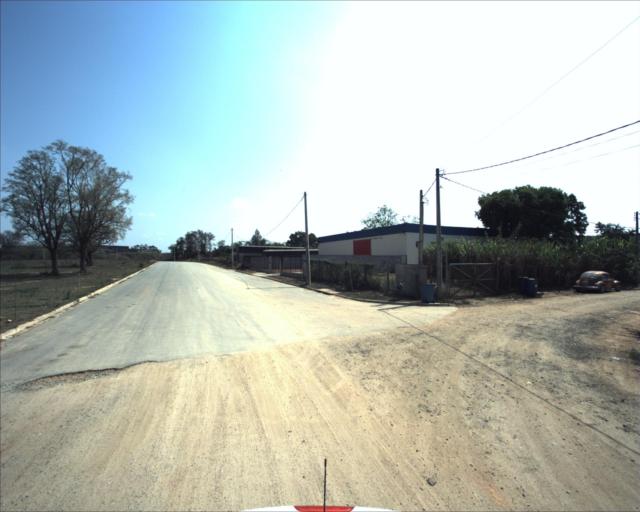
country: BR
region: Sao Paulo
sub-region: Sorocaba
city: Sorocaba
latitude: -23.4187
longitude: -47.4428
